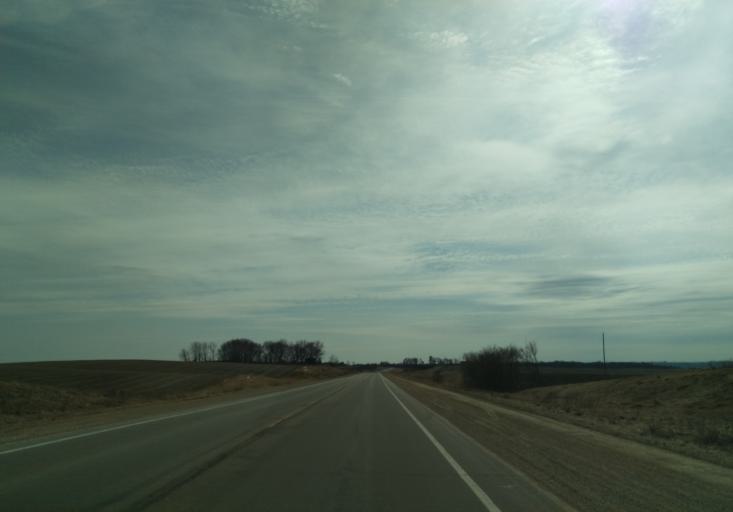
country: US
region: Iowa
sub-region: Winneshiek County
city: Decorah
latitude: 43.3623
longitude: -91.8042
